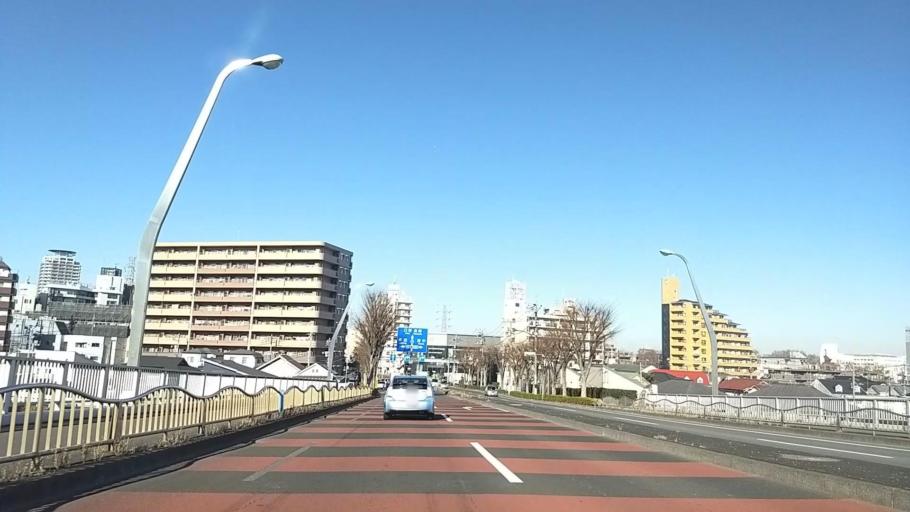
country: JP
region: Tokyo
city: Kokubunji
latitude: 35.6473
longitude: 139.4553
